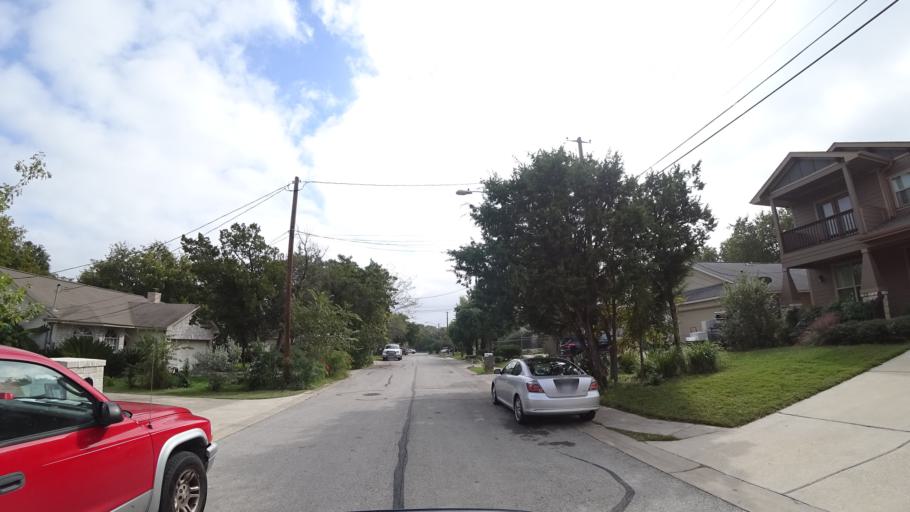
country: US
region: Texas
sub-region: Travis County
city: Shady Hollow
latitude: 30.2021
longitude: -97.8346
